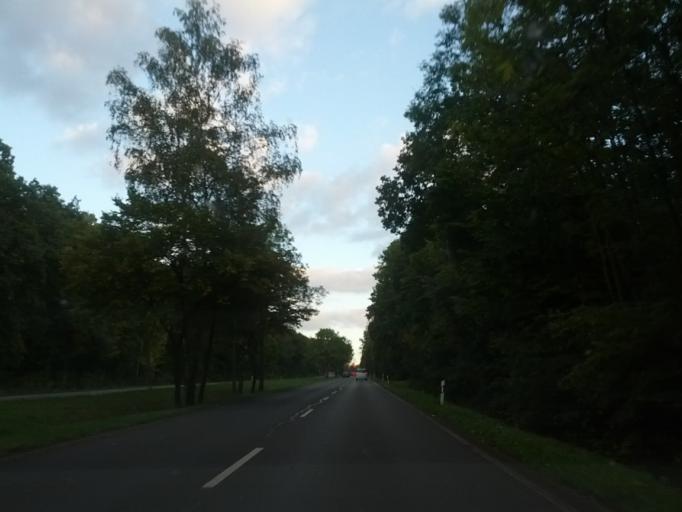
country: DE
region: Thuringia
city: Erfurt
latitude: 50.9462
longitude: 11.0298
